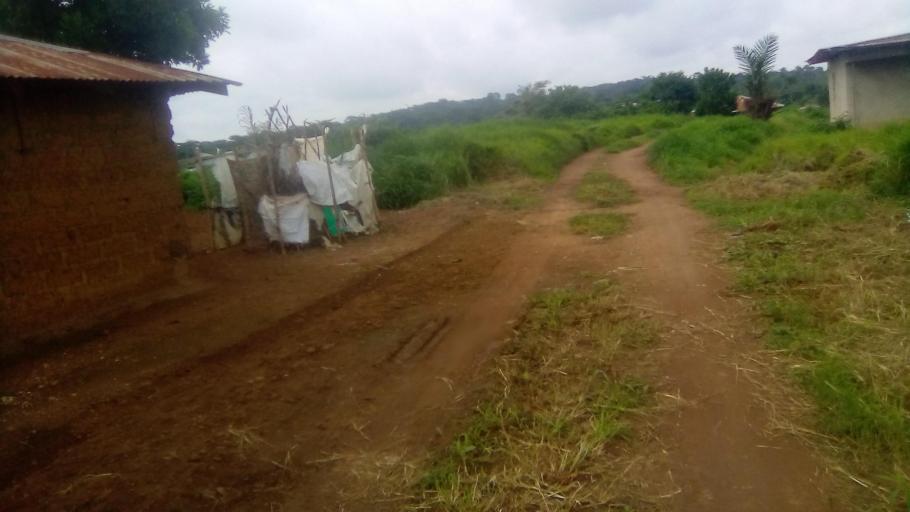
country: SL
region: Eastern Province
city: Kailahun
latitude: 8.2714
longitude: -10.5689
